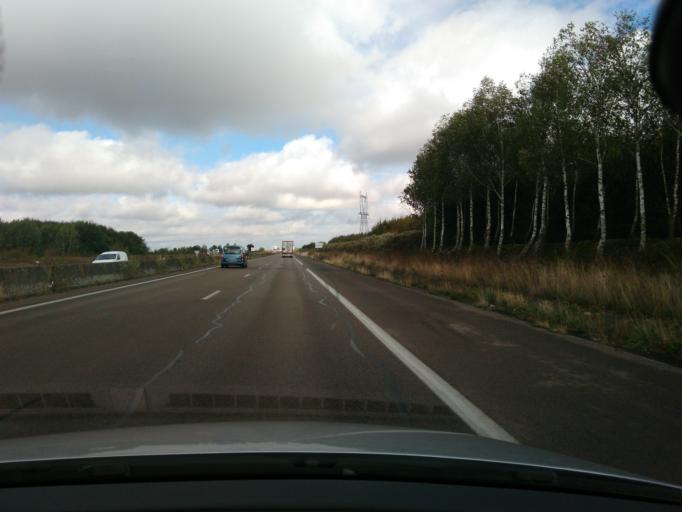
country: FR
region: Haute-Normandie
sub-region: Departement de l'Eure
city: La Madeleine-de-Nonancourt
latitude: 48.8505
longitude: 1.1802
